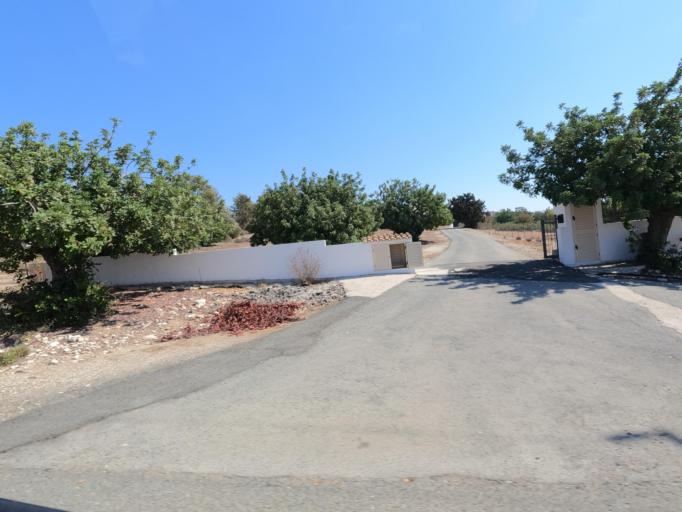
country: CY
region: Pafos
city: Paphos
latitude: 34.7774
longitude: 32.4540
